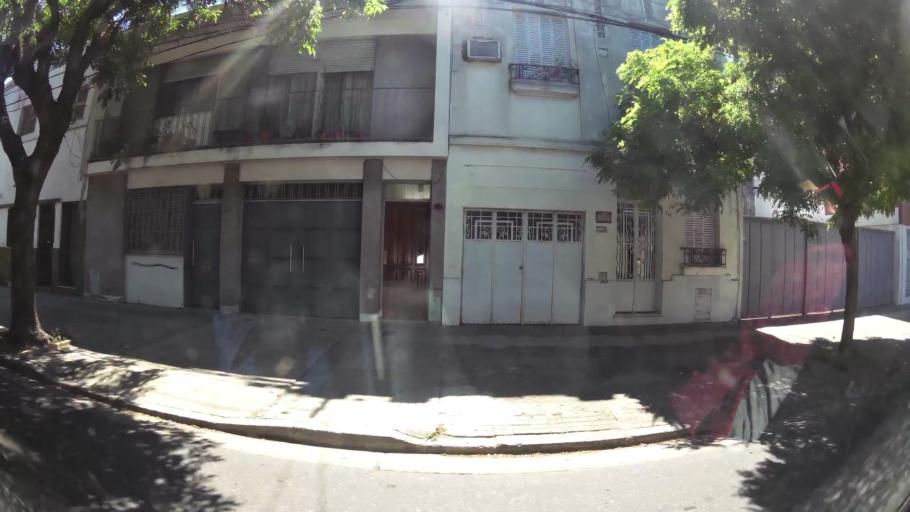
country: AR
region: Santa Fe
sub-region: Departamento de Rosario
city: Rosario
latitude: -32.9364
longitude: -60.6614
